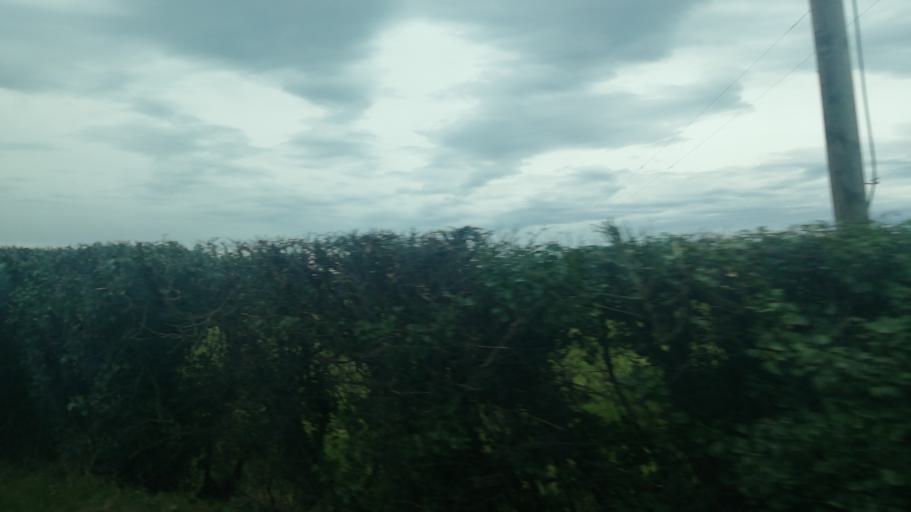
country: IE
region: Leinster
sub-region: Kildare
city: Clane
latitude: 53.3062
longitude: -6.6628
